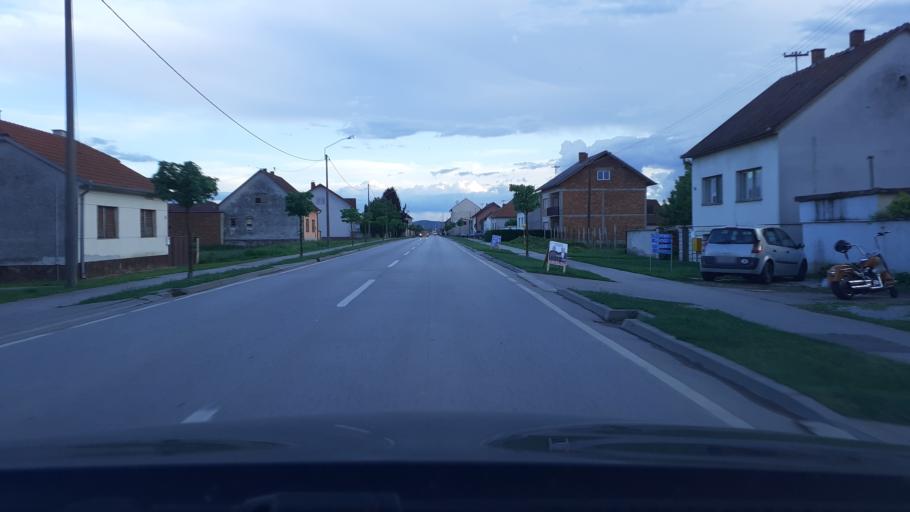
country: HR
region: Pozesko-Slavonska
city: Pleternica
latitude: 45.2941
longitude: 17.8077
